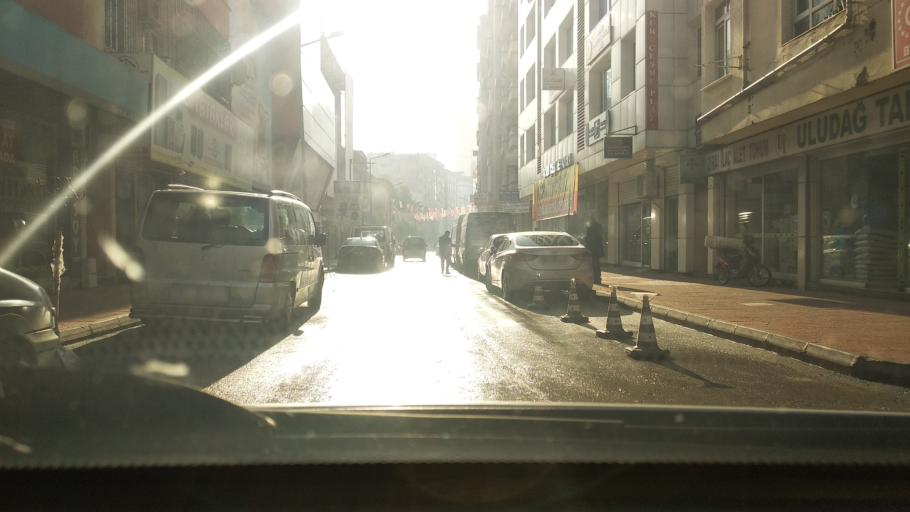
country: TR
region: Mersin
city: Mercin
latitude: 36.8060
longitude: 34.6222
